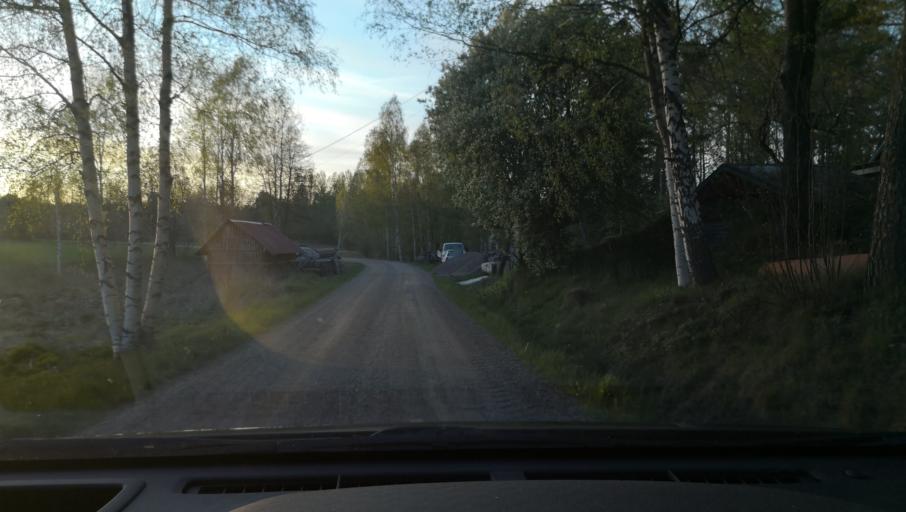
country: SE
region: OErebro
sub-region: Askersunds Kommun
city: Asbro
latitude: 58.9719
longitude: 14.9510
